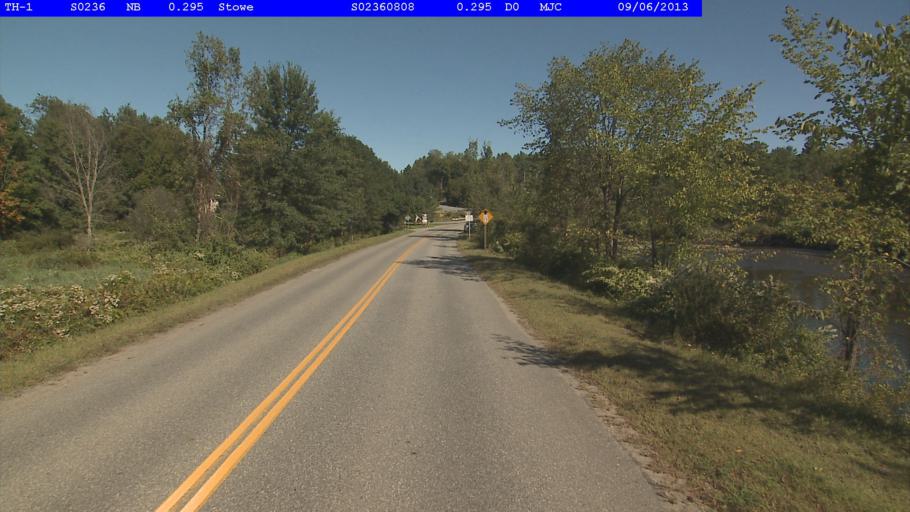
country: US
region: Vermont
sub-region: Washington County
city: Waterbury
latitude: 44.4392
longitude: -72.7140
